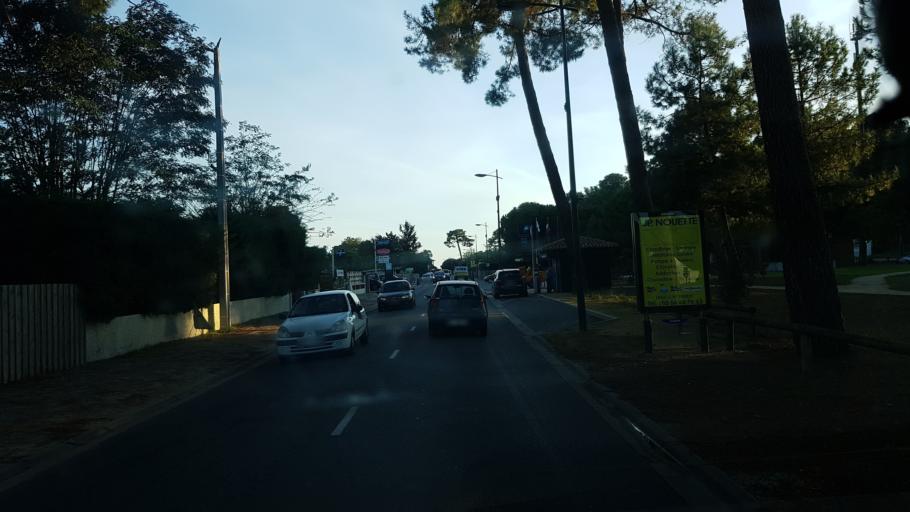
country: FR
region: Aquitaine
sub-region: Departement de la Gironde
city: Ares
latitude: 44.7477
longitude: -1.1811
